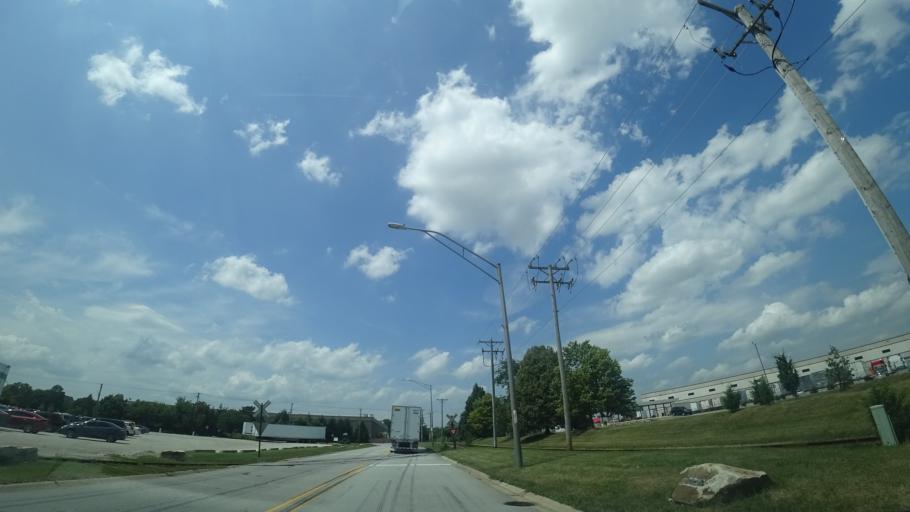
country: US
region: Illinois
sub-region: Cook County
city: Crestwood
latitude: 41.6716
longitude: -87.7571
